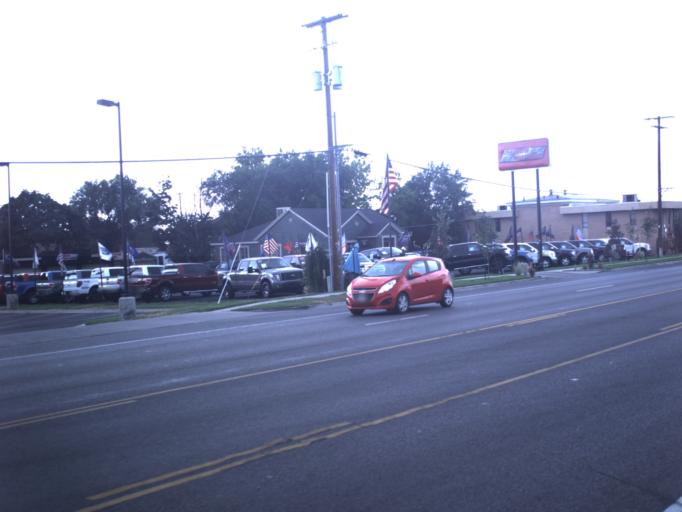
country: US
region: Utah
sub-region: Salt Lake County
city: Midvale
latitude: 40.6026
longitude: -111.8907
